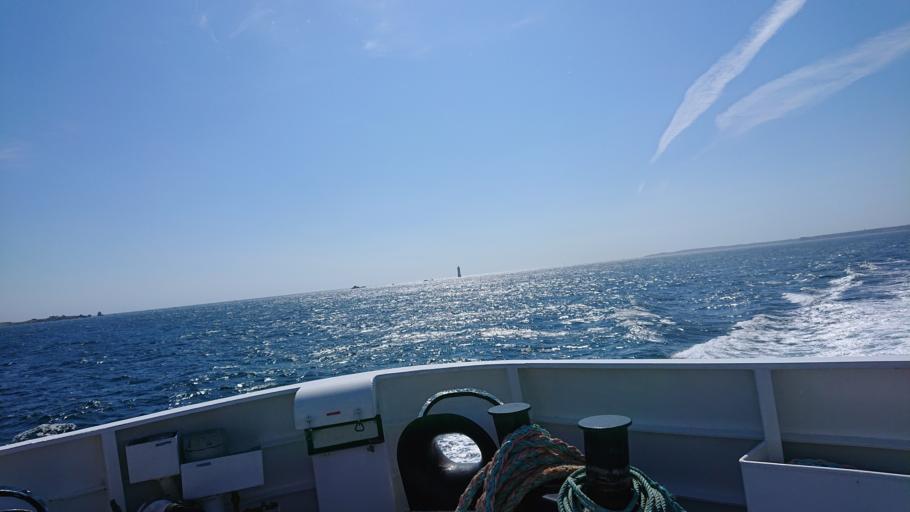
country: FR
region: Brittany
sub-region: Departement du Finistere
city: Lampaul-Plouarzel
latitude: 48.4460
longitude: -4.9972
